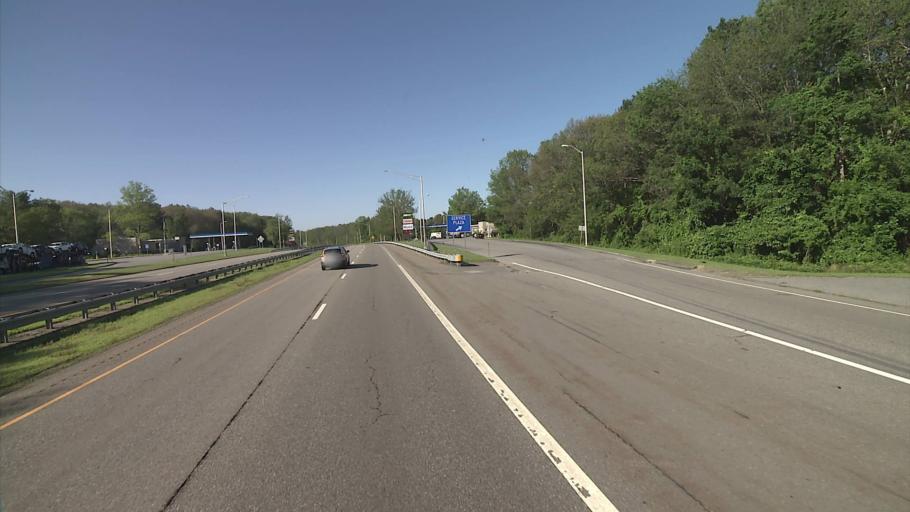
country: US
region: Connecticut
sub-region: Windham County
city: Wauregan
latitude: 41.7555
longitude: -71.8771
